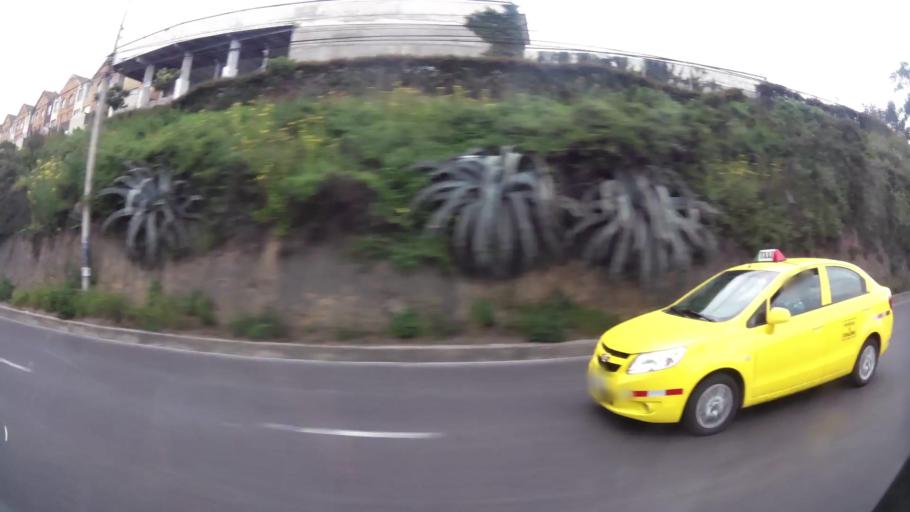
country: EC
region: Pichincha
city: Quito
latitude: -0.0978
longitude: -78.4648
